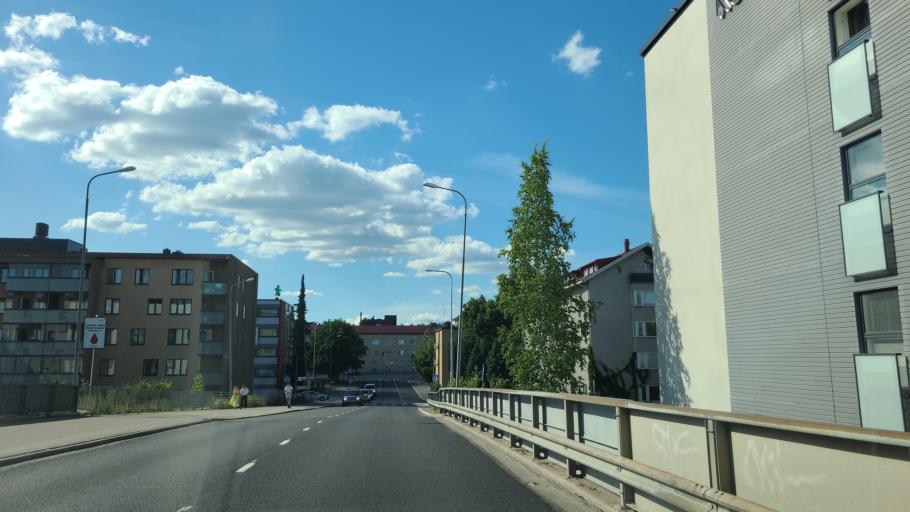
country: FI
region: Central Finland
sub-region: Jyvaeskylae
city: Jyvaeskylae
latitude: 62.2447
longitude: 25.7611
